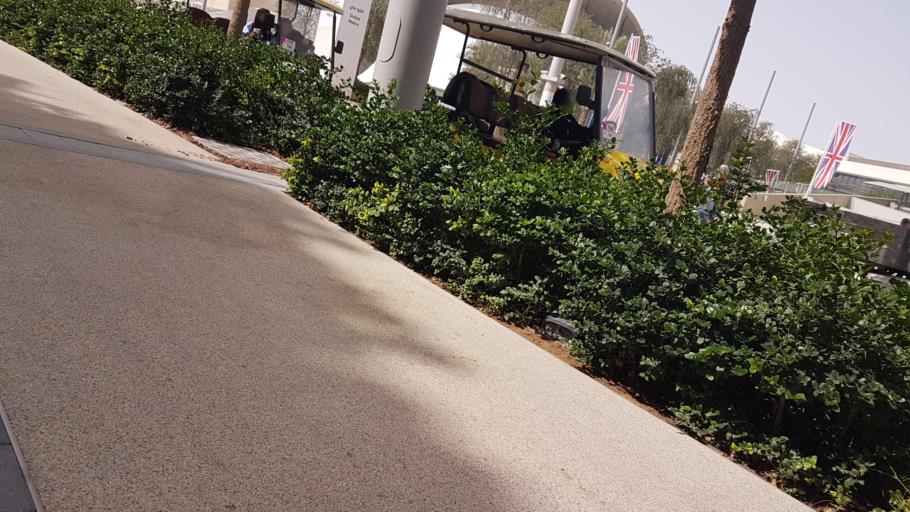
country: AE
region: Dubai
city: Dubai
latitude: 24.9638
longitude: 55.1508
